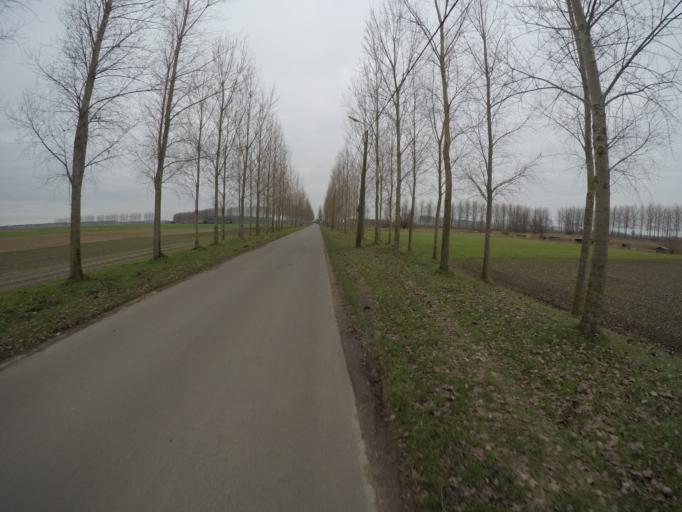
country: BE
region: Flanders
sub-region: Provincie Oost-Vlaanderen
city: Sint-Gillis-Waas
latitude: 51.2422
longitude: 4.1262
